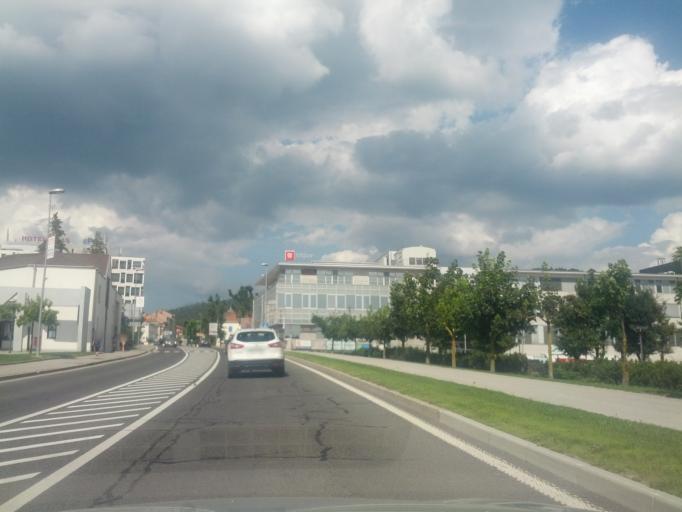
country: SI
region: Postojna
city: Postojna
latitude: 45.7732
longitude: 14.2112
